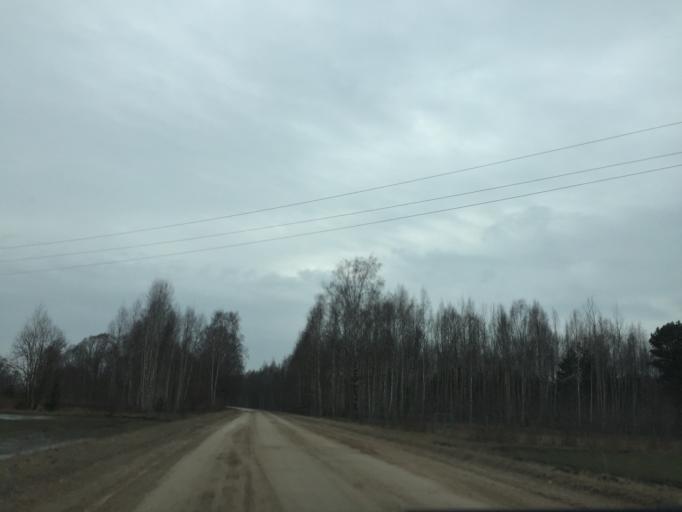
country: LV
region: Ozolnieku
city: Ozolnieki
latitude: 56.7056
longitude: 23.7662
